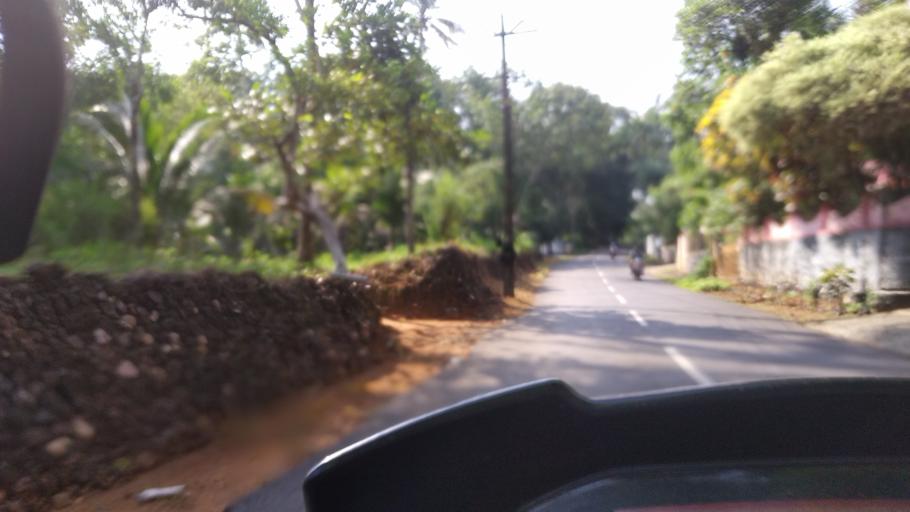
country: IN
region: Kerala
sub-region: Kottayam
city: Palackattumala
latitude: 9.8008
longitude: 76.5834
